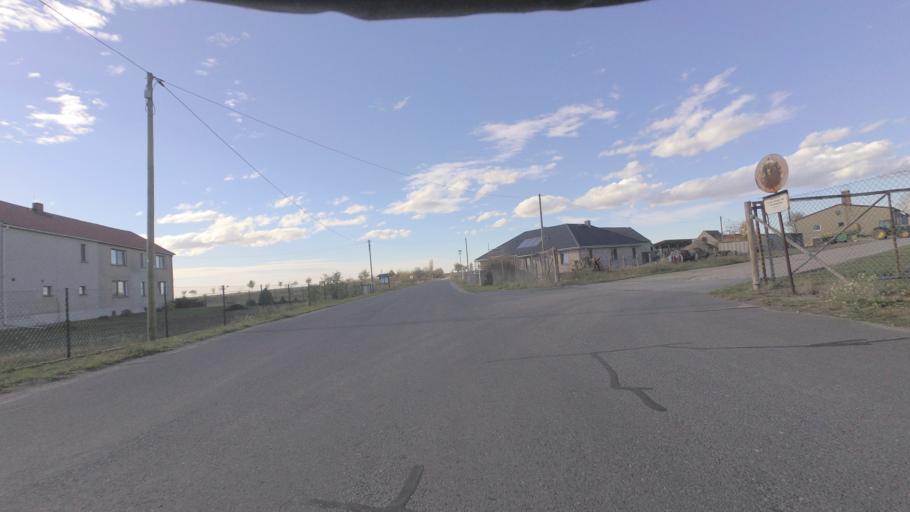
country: DE
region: Saxony
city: Nauwalde
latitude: 51.4538
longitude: 13.3350
